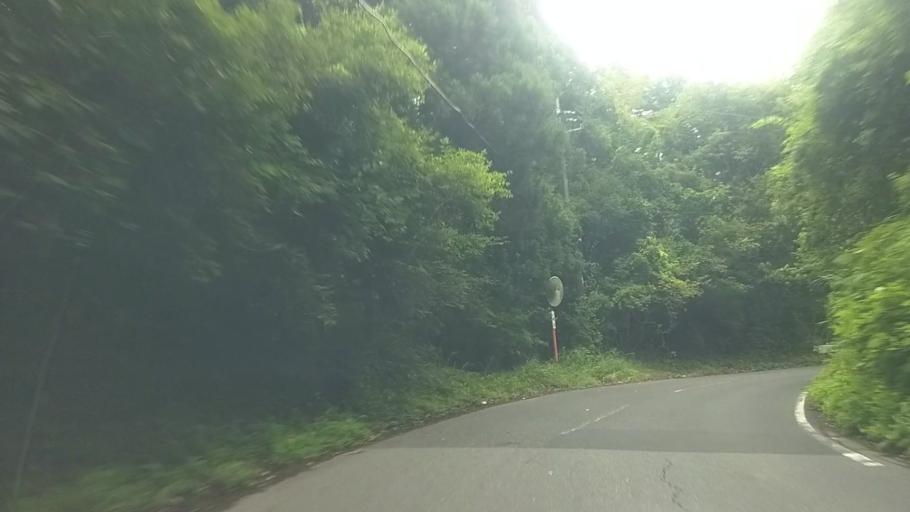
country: JP
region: Chiba
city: Kawaguchi
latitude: 35.2268
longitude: 140.0278
